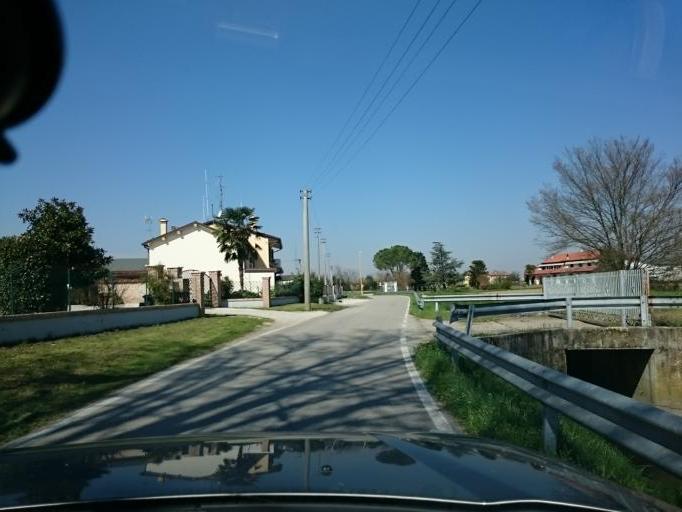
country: IT
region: Veneto
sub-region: Provincia di Padova
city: Ponte San Nicolo
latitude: 45.3663
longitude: 11.9015
